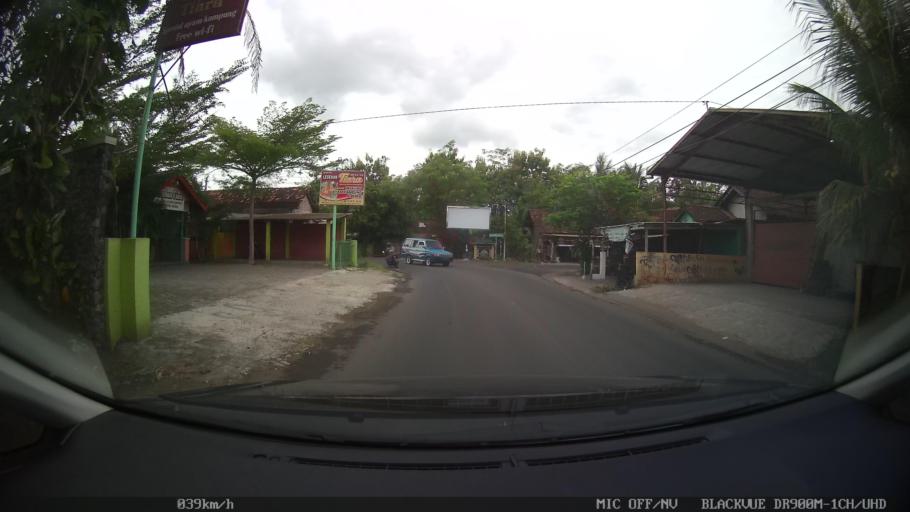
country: ID
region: Daerah Istimewa Yogyakarta
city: Sewon
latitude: -7.8754
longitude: 110.4069
